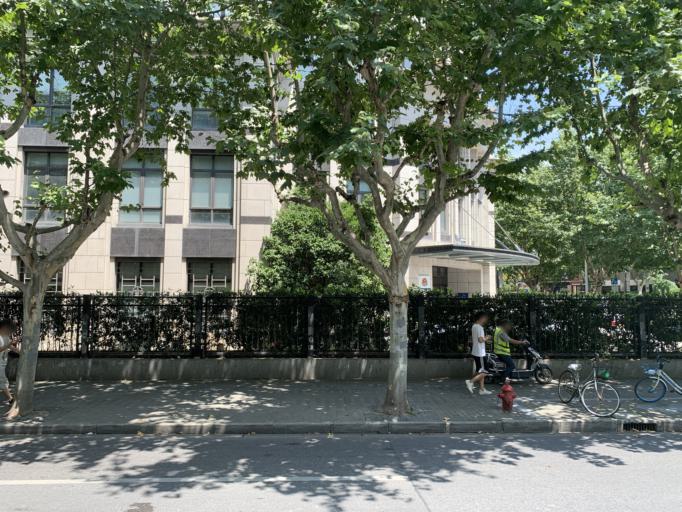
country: CN
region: Shanghai Shi
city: Pudong
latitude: 31.2454
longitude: 121.5419
